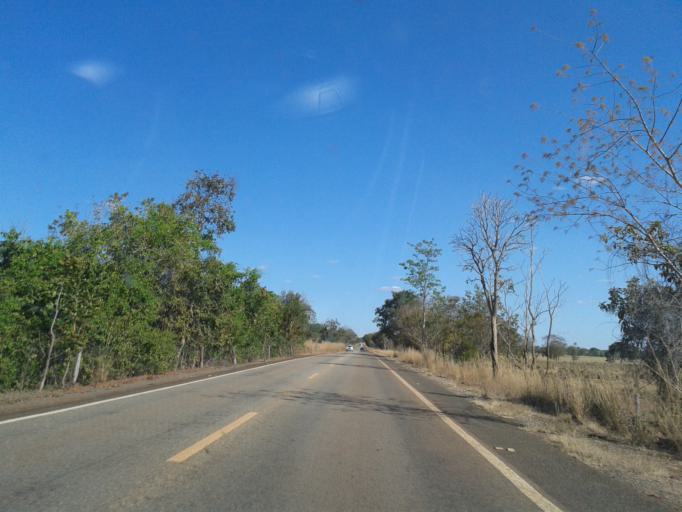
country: BR
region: Goias
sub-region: Mozarlandia
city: Mozarlandia
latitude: -14.2855
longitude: -50.4017
